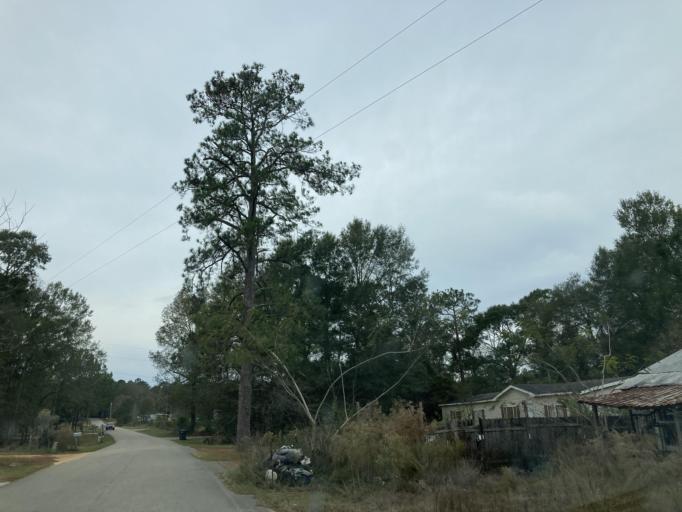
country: US
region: Mississippi
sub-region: Lamar County
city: Purvis
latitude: 31.1188
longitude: -89.4585
